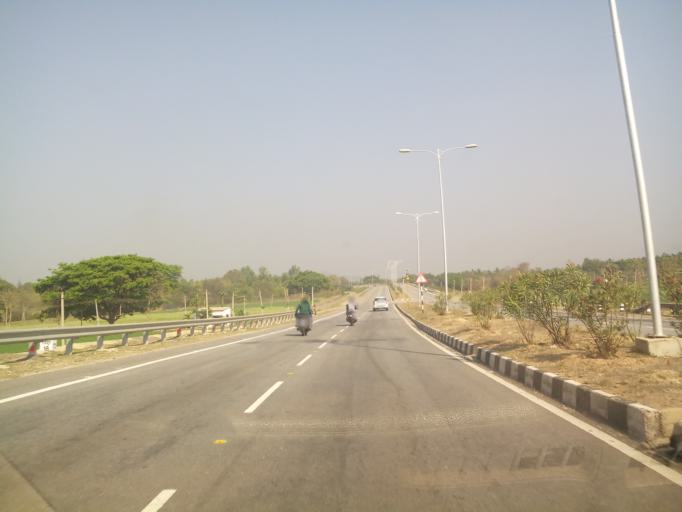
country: IN
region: Karnataka
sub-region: Tumkur
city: Kunigal
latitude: 13.0012
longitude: 77.0189
